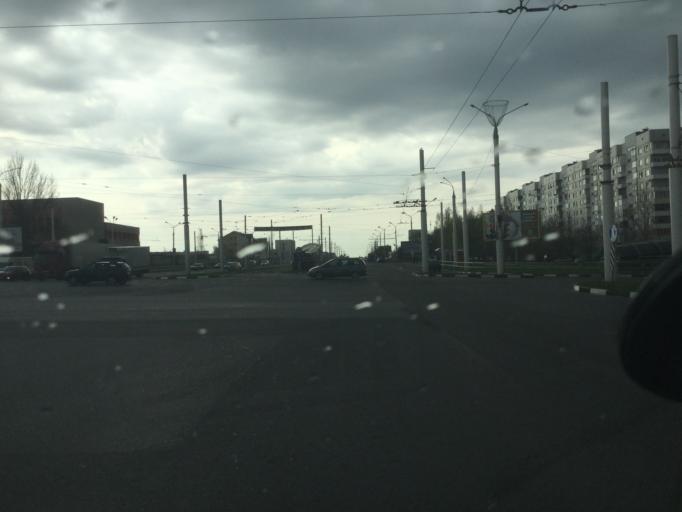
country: BY
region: Vitebsk
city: Vitebsk
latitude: 55.1763
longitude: 30.2448
